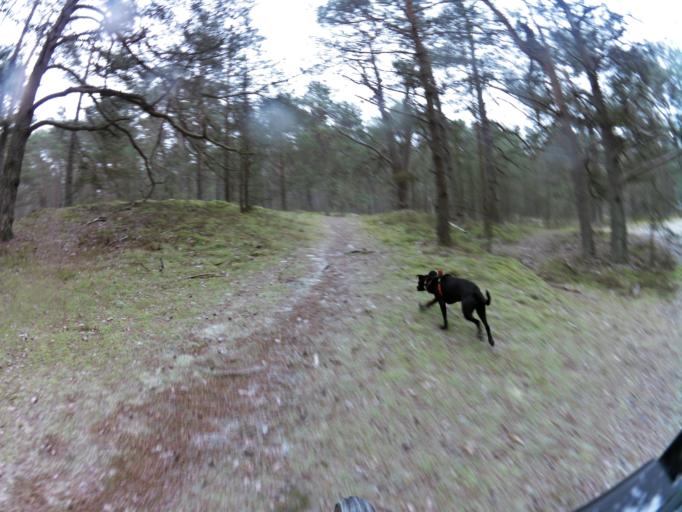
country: PL
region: West Pomeranian Voivodeship
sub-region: Powiat gryficki
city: Cerkwica
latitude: 54.1073
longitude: 15.1322
